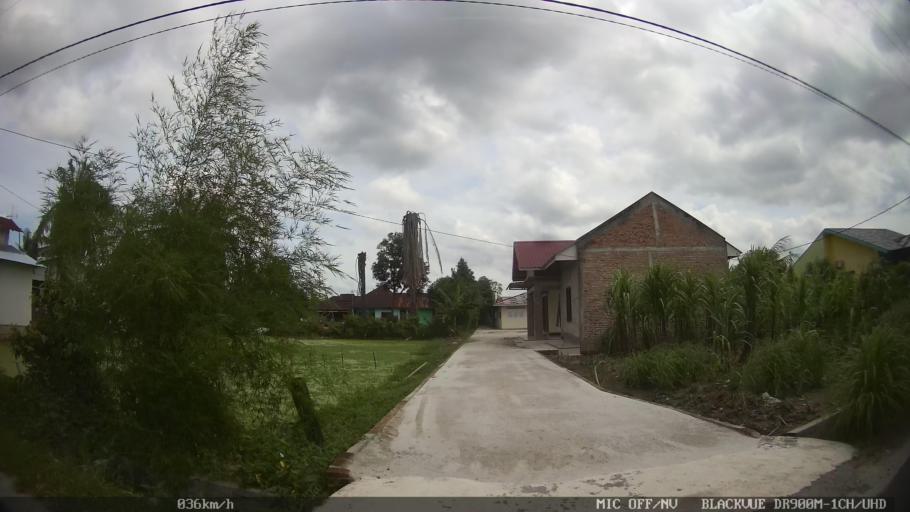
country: ID
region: North Sumatra
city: Percut
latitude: 3.5686
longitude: 98.8625
